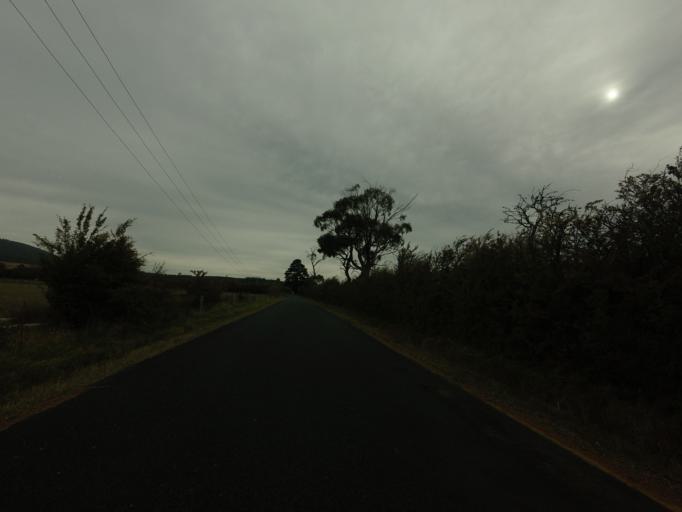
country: AU
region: Tasmania
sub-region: Sorell
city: Sorell
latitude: -42.6394
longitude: 147.5621
